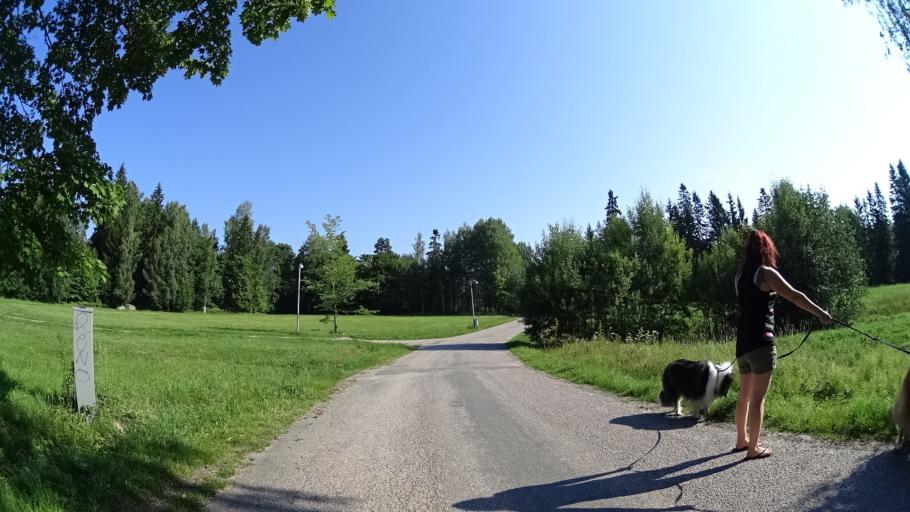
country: FI
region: Uusimaa
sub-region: Helsinki
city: Vantaa
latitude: 60.3181
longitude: 25.0814
